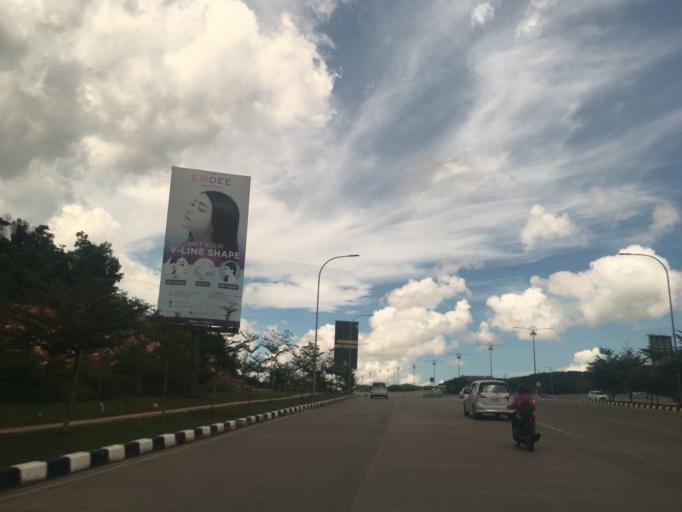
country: SG
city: Singapore
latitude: 1.1266
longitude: 104.0176
